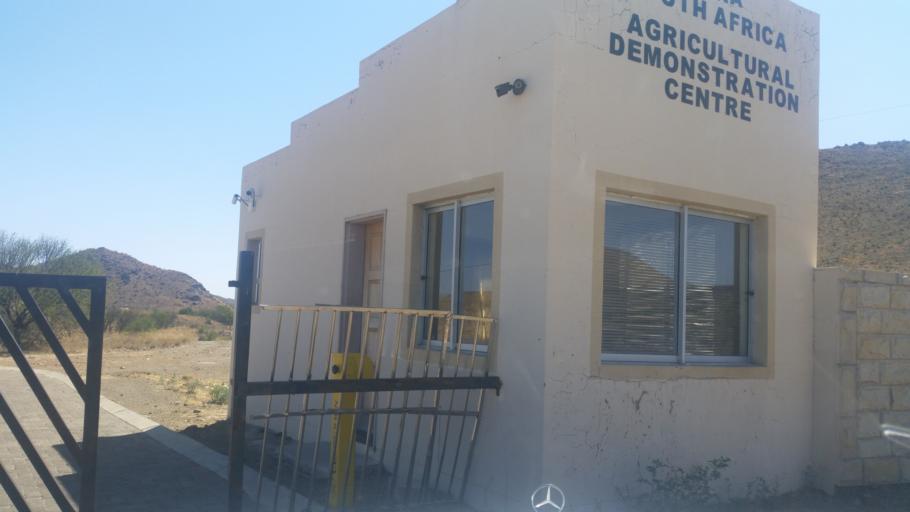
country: ZA
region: Northern Cape
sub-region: Pixley ka Seme District Municipality
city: Colesberg
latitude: -30.6244
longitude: 25.4758
